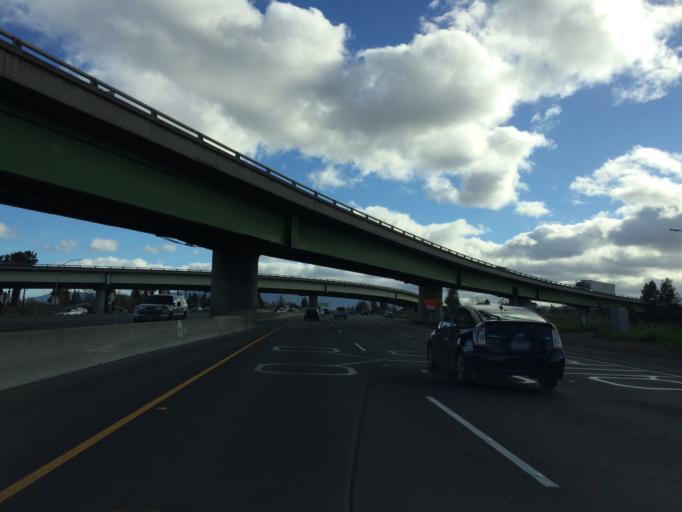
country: US
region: California
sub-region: Santa Clara County
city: Burbank
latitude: 37.3193
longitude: -121.9403
